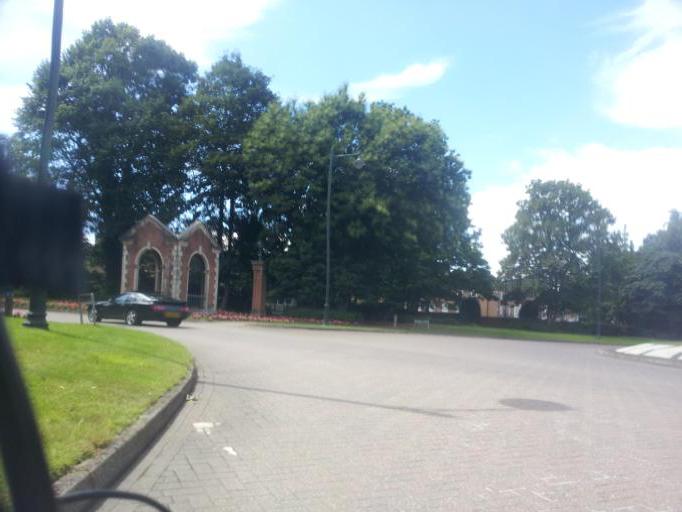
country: GB
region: England
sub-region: Kent
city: Kings Hill
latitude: 51.2742
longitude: 0.3940
